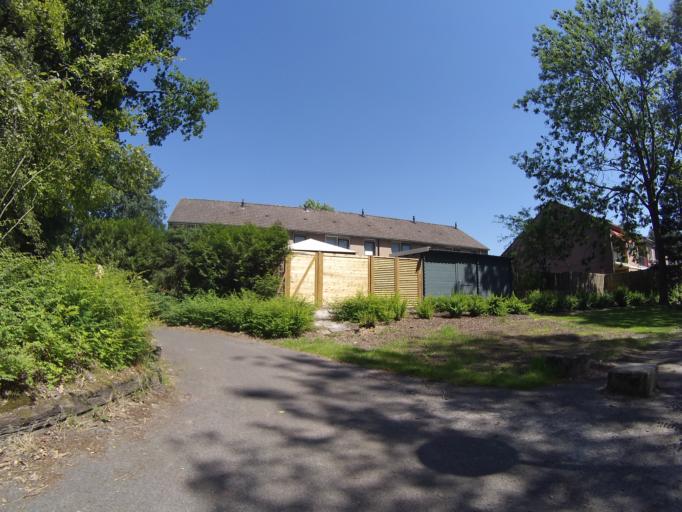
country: NL
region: Drenthe
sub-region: Gemeente Emmen
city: Emmen
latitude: 52.7677
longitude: 6.8851
